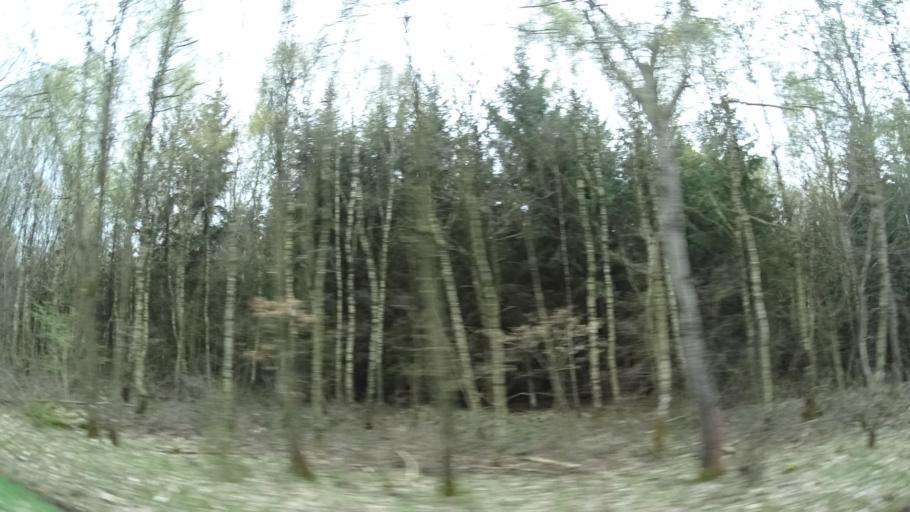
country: DE
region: Rheinland-Pfalz
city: Weitersborn
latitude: 49.8748
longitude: 7.5327
